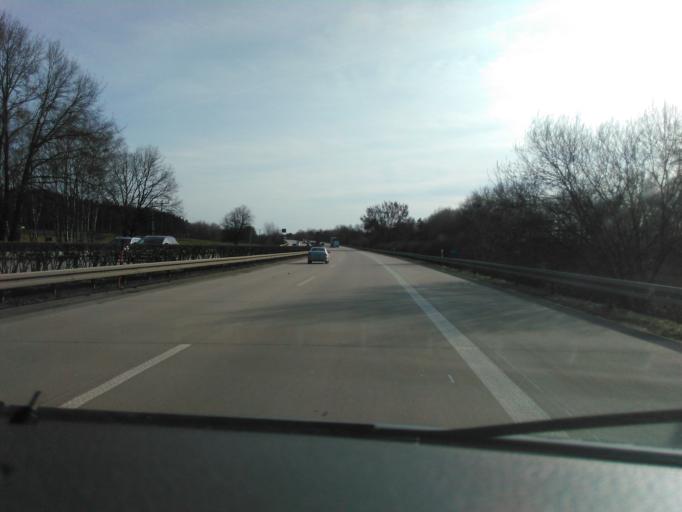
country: DE
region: Brandenburg
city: Schipkau
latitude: 51.5273
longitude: 13.9053
